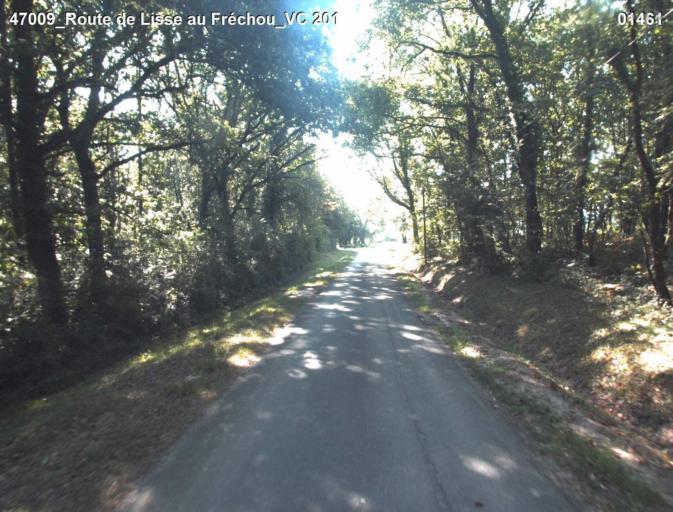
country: FR
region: Aquitaine
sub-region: Departement du Lot-et-Garonne
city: Mezin
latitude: 44.0925
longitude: 0.2941
